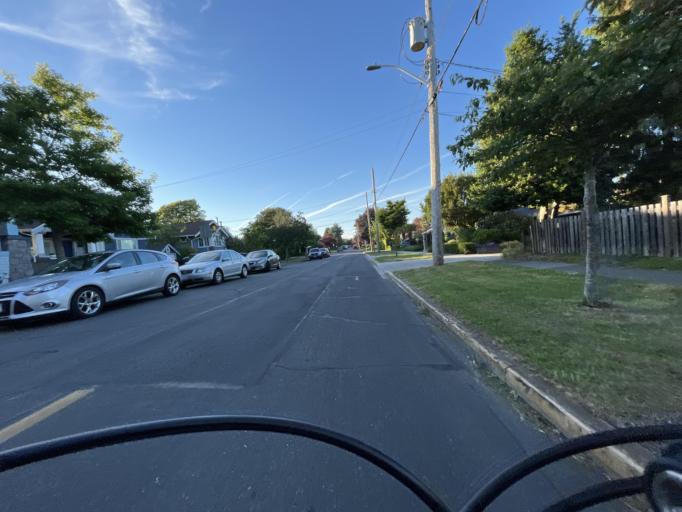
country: CA
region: British Columbia
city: Victoria
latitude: 48.4104
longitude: -123.3316
